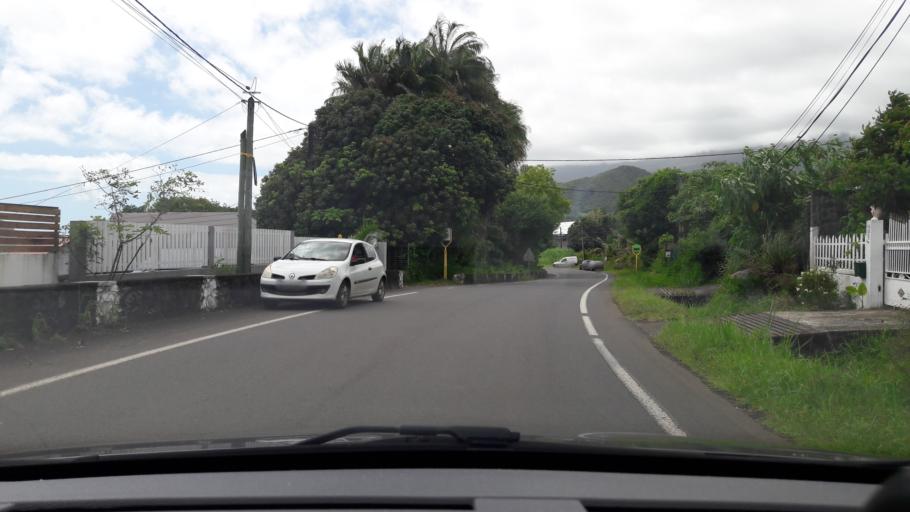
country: RE
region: Reunion
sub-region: Reunion
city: Saint-Benoit
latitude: -21.0880
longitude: 55.7003
